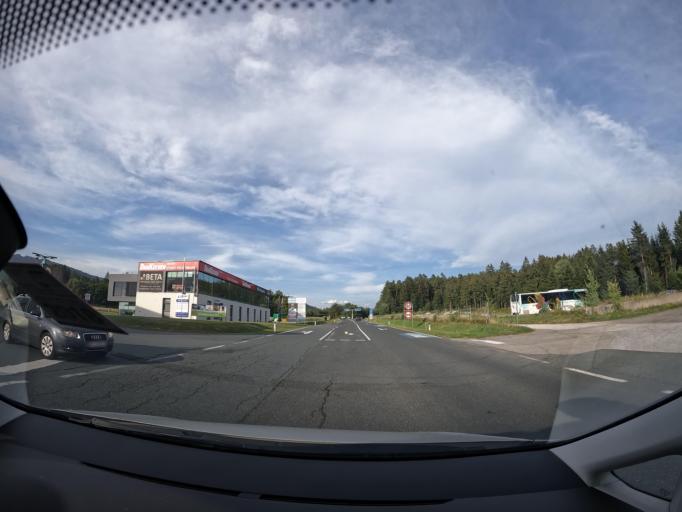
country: AT
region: Carinthia
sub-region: Politischer Bezirk Volkermarkt
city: Voelkermarkt
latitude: 46.6812
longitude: 14.6776
